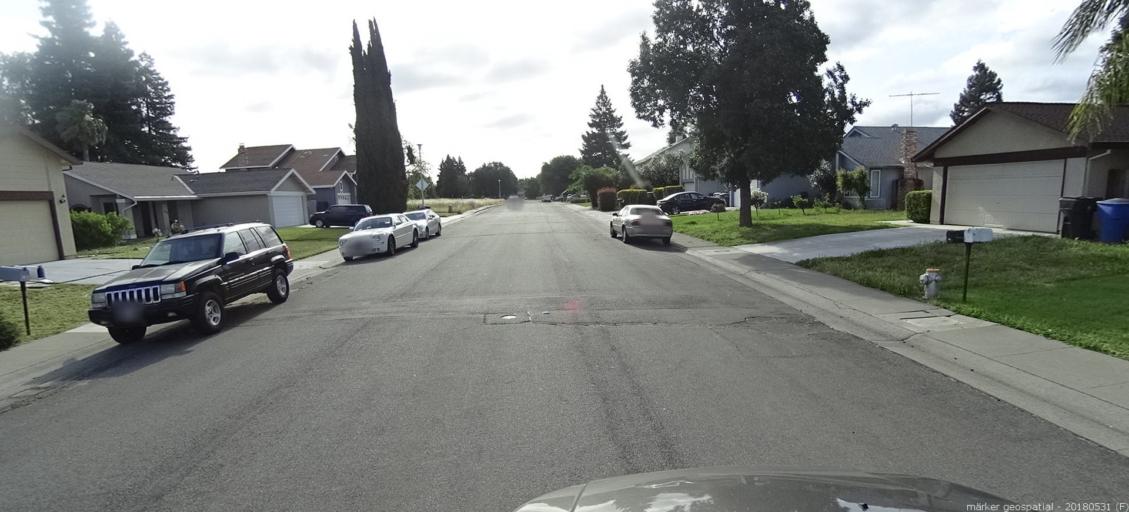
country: US
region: California
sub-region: Sacramento County
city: Sacramento
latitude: 38.6290
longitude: -121.4913
